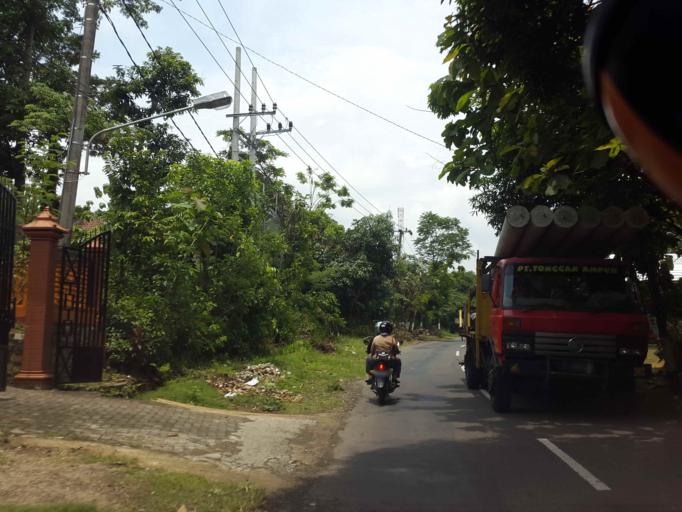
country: ID
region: East Java
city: Ponorogo
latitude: -7.7213
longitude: 111.3563
